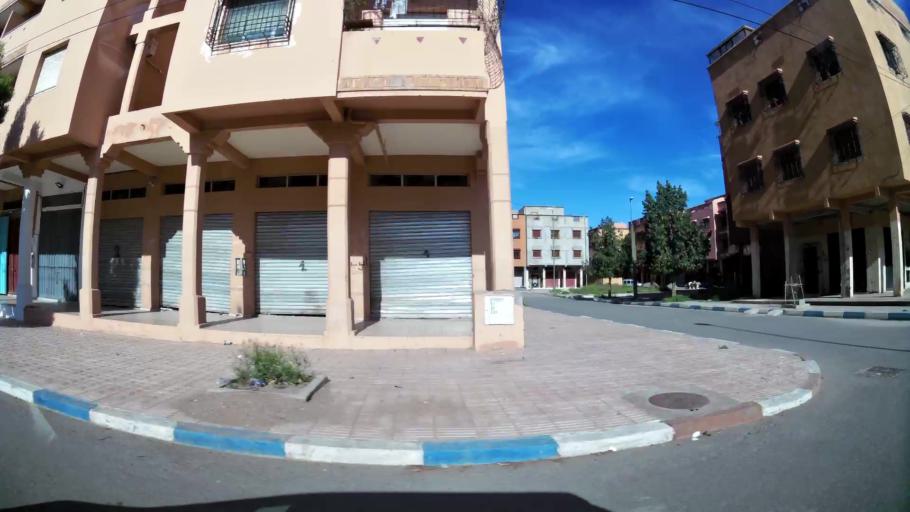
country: MA
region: Marrakech-Tensift-Al Haouz
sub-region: Marrakech
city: Marrakesh
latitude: 31.6883
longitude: -8.0750
